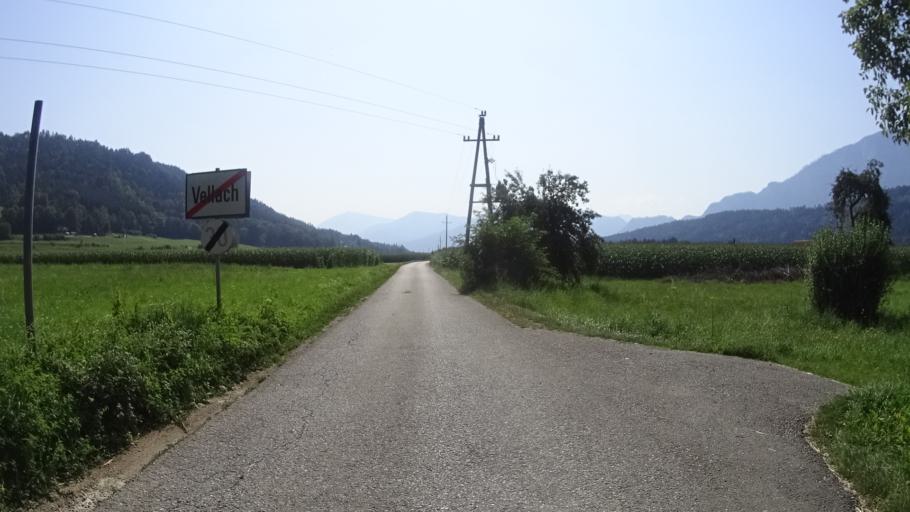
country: AT
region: Carinthia
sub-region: Politischer Bezirk Volkermarkt
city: Gallizien
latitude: 46.5708
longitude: 14.5178
